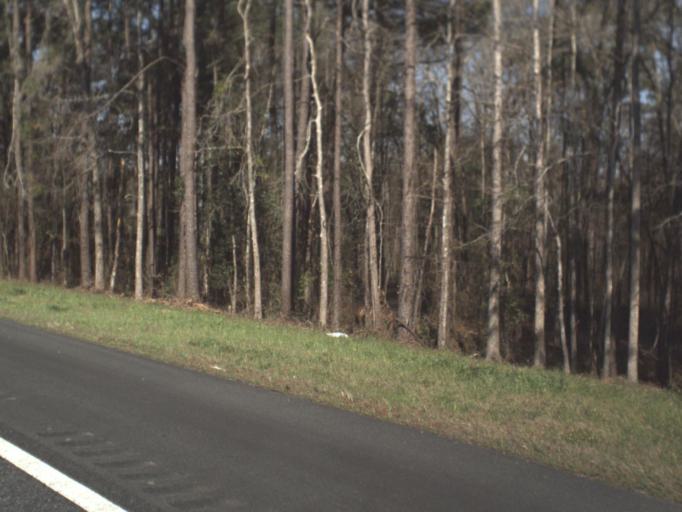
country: US
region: Florida
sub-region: Leon County
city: Tallahassee
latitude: 30.4985
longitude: -84.1914
